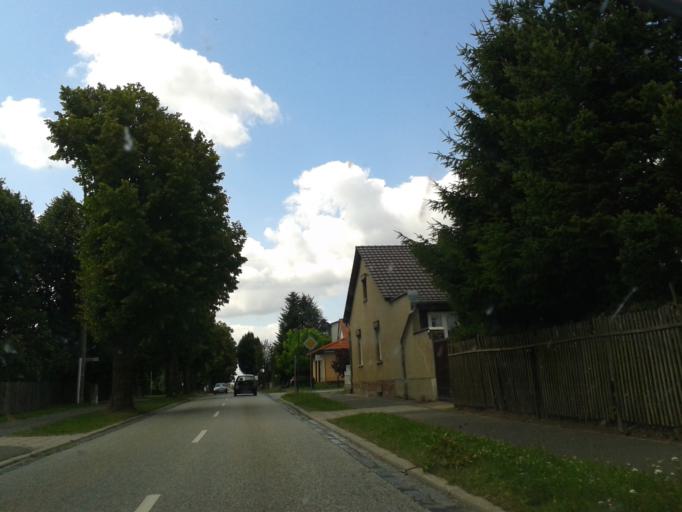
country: DE
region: Saxony-Anhalt
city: Klostermansfeld
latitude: 51.5792
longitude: 11.4944
